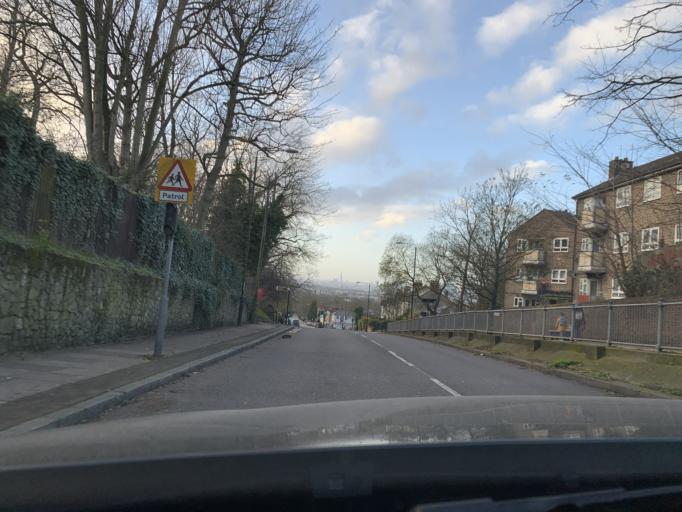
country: GB
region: England
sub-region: Greater London
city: Woolwich
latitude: 51.4698
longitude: 0.0625
